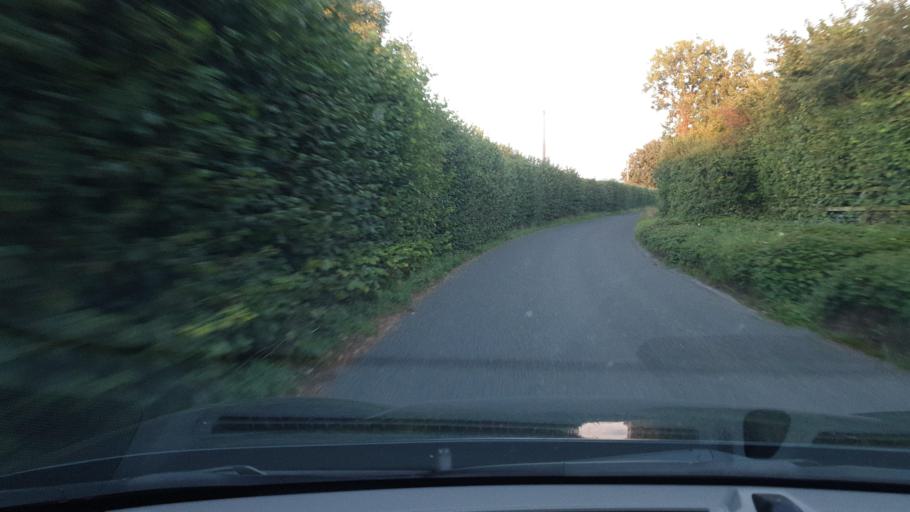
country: IE
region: Leinster
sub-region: Kildare
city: Prosperous
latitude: 53.3249
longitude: -6.7938
